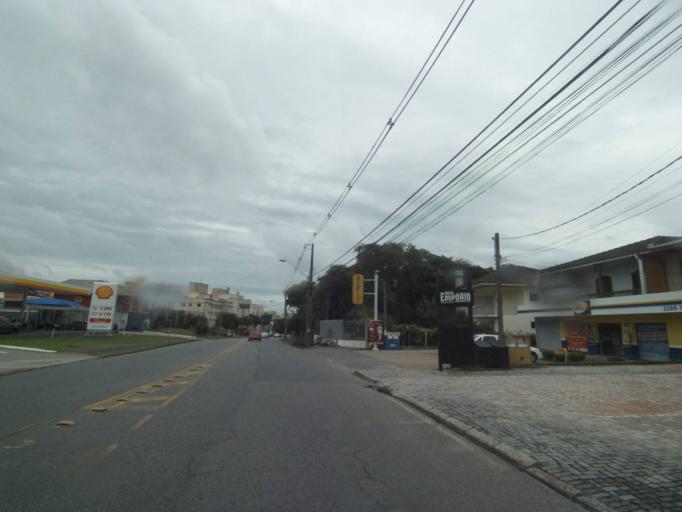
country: BR
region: Parana
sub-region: Curitiba
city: Curitiba
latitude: -25.4607
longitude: -49.3344
